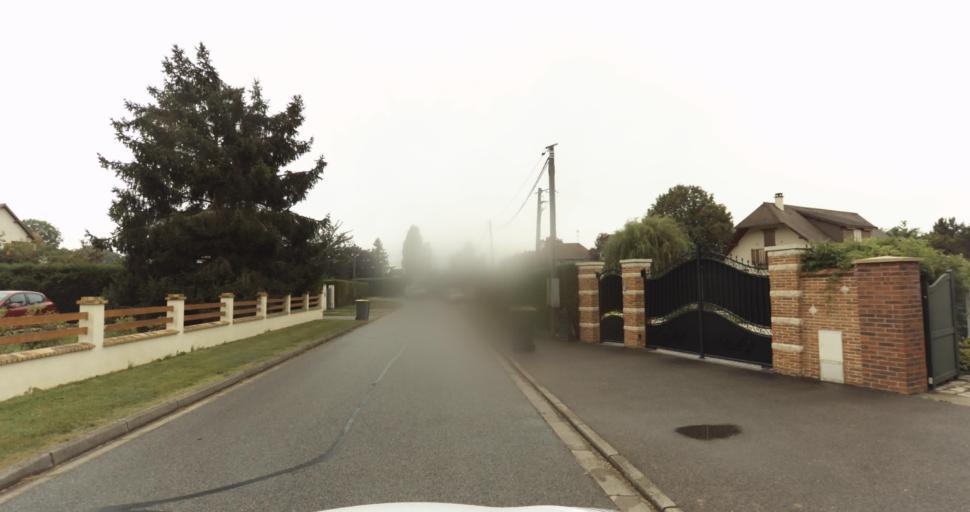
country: FR
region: Haute-Normandie
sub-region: Departement de l'Eure
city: Normanville
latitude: 49.0969
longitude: 1.1515
